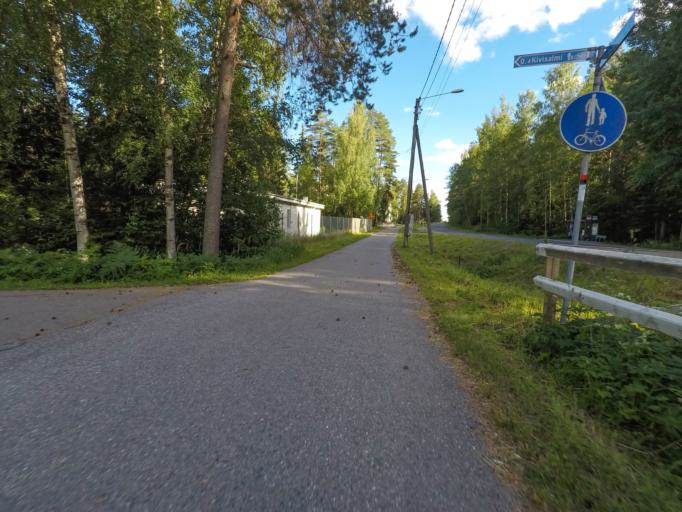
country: FI
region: South Karelia
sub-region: Lappeenranta
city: Lappeenranta
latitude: 61.0845
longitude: 28.1470
